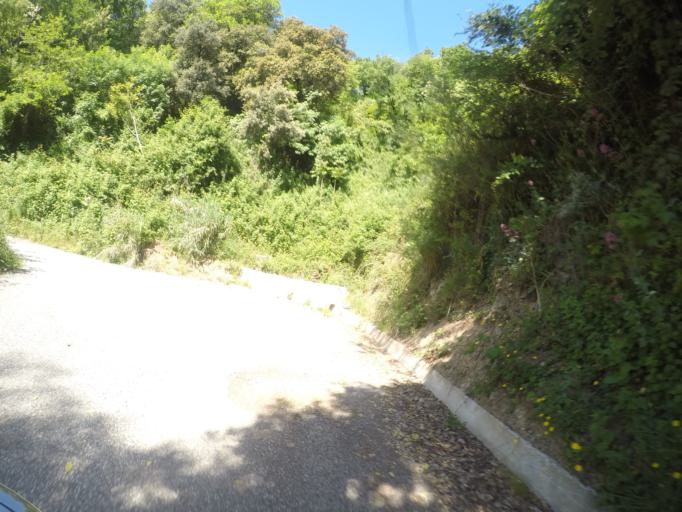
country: IT
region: Tuscany
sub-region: Provincia di Massa-Carrara
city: Massa
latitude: 44.0513
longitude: 10.1033
